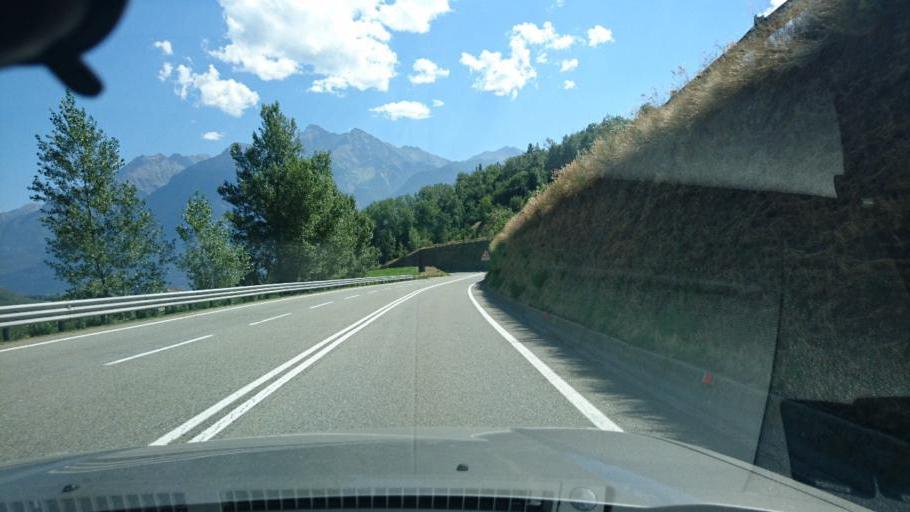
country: IT
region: Aosta Valley
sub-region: Valle d'Aosta
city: Gignod
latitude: 45.7688
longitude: 7.3048
